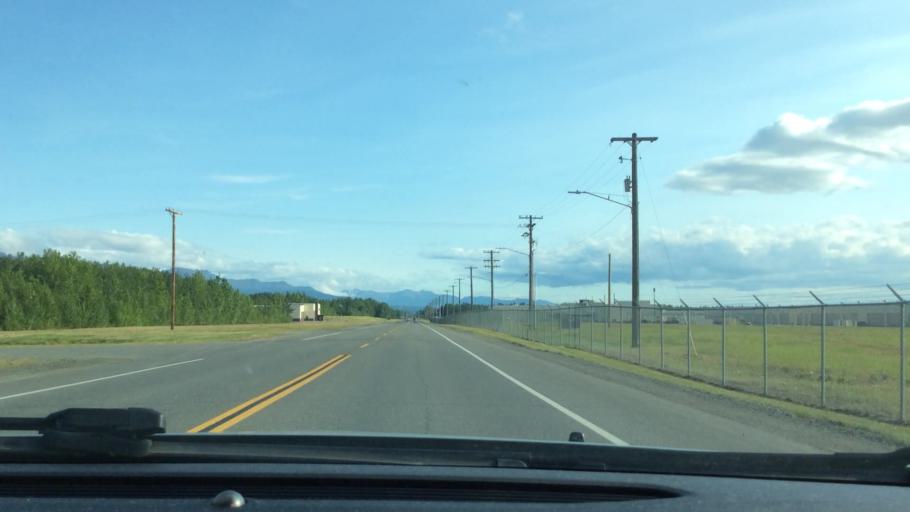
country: US
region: Alaska
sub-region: Anchorage Municipality
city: Anchorage
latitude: 61.2506
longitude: -149.7785
